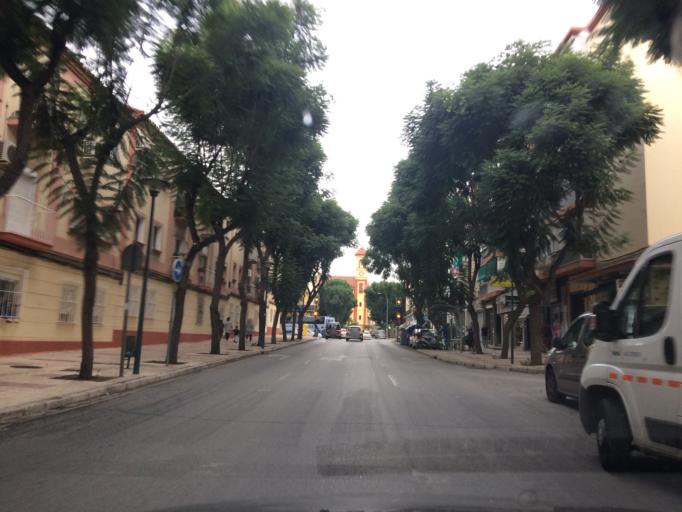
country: ES
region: Andalusia
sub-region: Provincia de Malaga
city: Malaga
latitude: 36.7151
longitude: -4.4428
